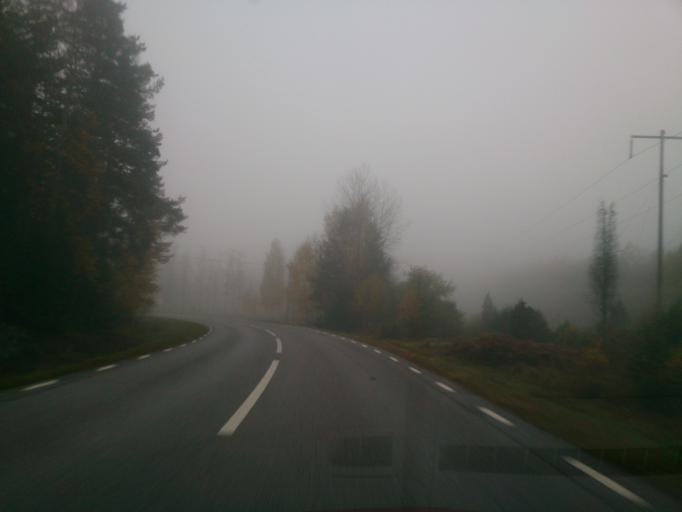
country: SE
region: OEstergoetland
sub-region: Atvidabergs Kommun
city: Atvidaberg
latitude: 58.1364
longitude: 15.9573
